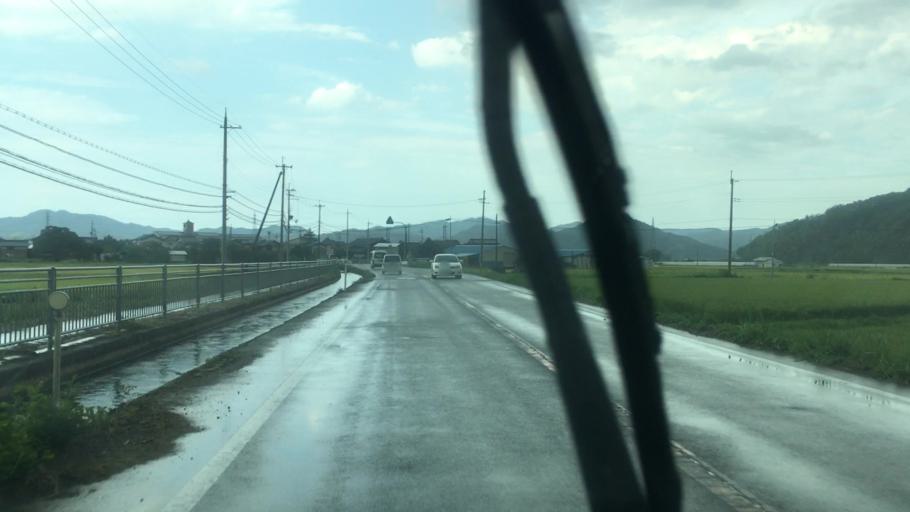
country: JP
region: Hyogo
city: Toyooka
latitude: 35.4981
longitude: 134.8173
